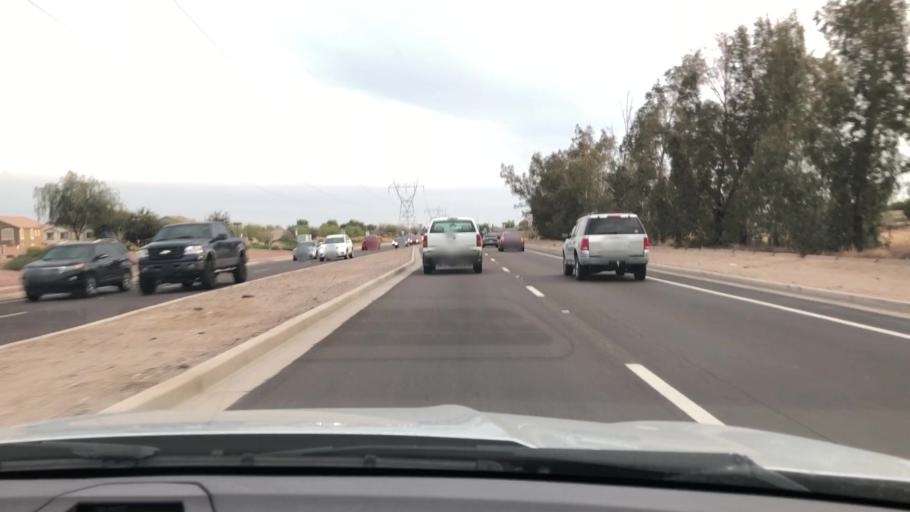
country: US
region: Arizona
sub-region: Pinal County
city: San Tan Valley
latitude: 33.2388
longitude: -111.5633
